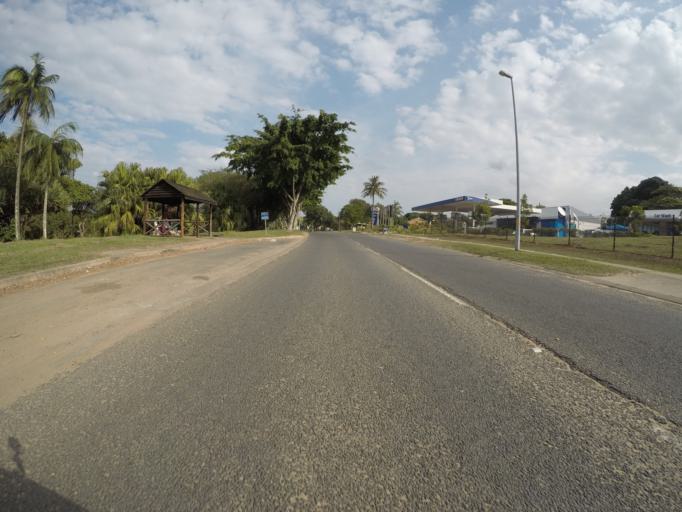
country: ZA
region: KwaZulu-Natal
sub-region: uThungulu District Municipality
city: Richards Bay
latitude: -28.7358
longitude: 32.0665
